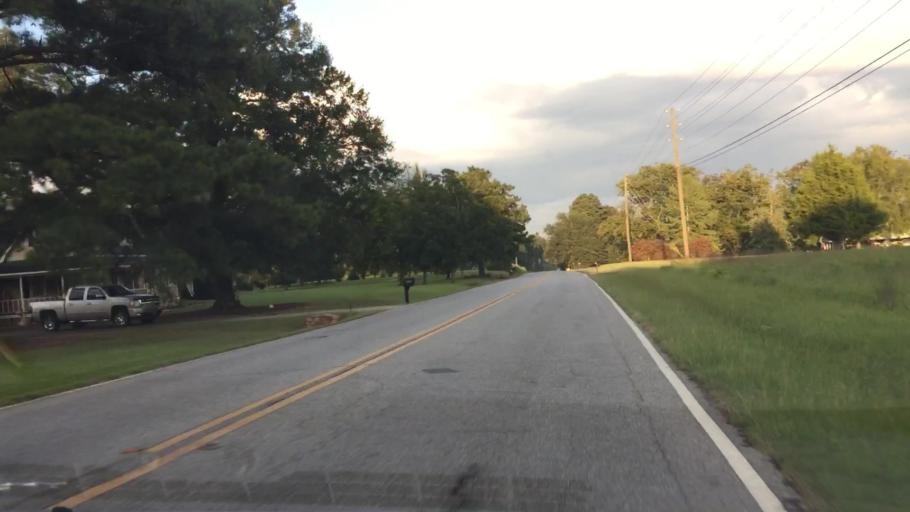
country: US
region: Georgia
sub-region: Henry County
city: McDonough
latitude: 33.4914
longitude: -84.1617
